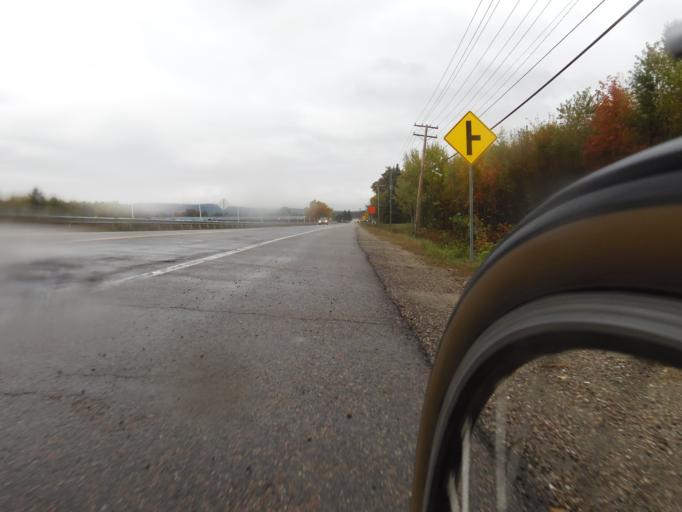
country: CA
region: Quebec
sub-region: Outaouais
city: Fort-Coulonge
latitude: 45.8577
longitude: -76.7398
